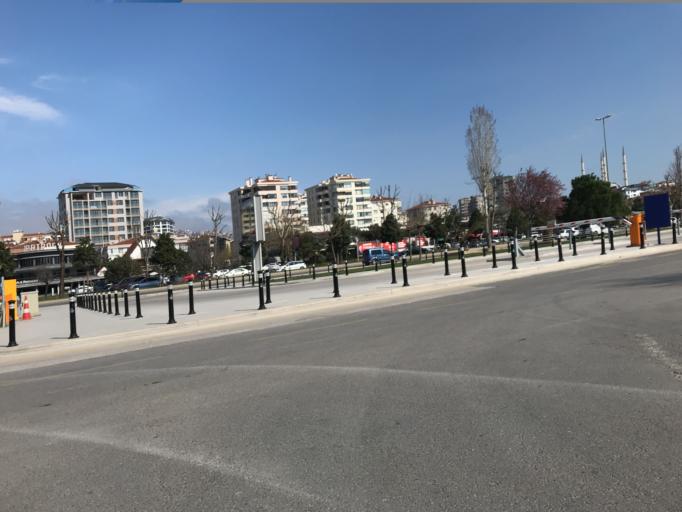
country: TR
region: Istanbul
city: Maltepe
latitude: 40.9272
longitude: 29.1214
